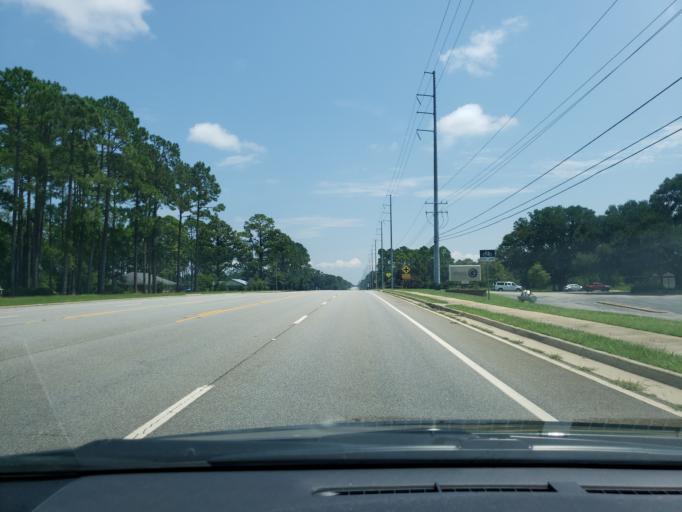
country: US
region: Georgia
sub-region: Dougherty County
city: Albany
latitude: 31.5856
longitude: -84.2796
